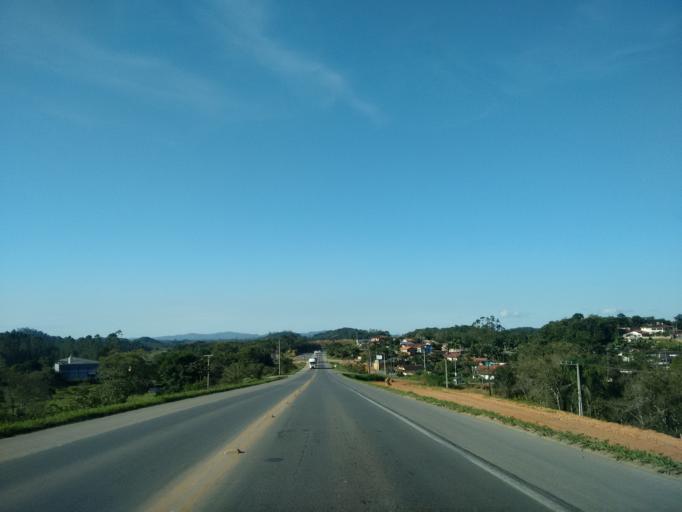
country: BR
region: Santa Catarina
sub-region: Guaramirim
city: Guaramirim
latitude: -26.4565
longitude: -48.9315
